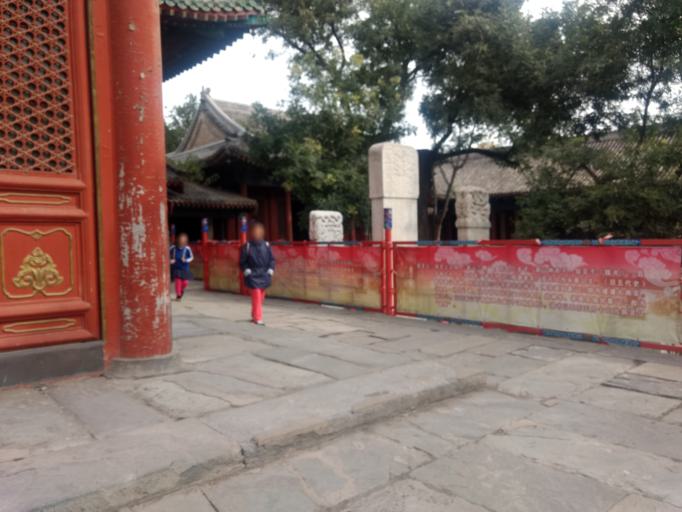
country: CN
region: Beijing
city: Chaowai
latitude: 39.9236
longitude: 116.4378
